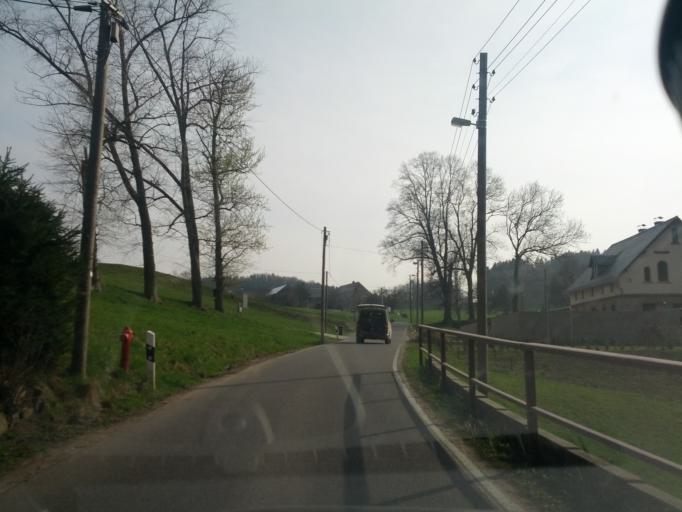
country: DE
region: Saxony
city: Kirchberg
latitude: 50.5853
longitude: 12.5138
